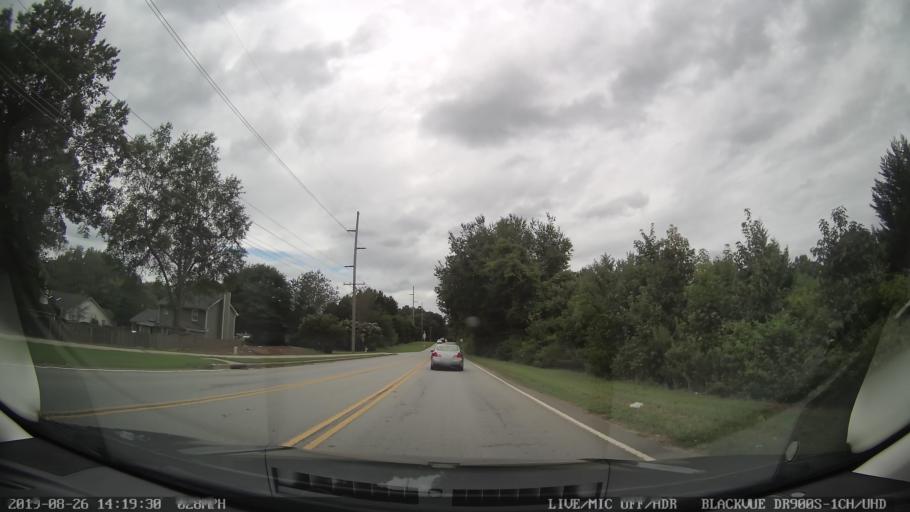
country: US
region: South Carolina
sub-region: Greenville County
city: Five Forks
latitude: 34.8014
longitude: -82.2429
